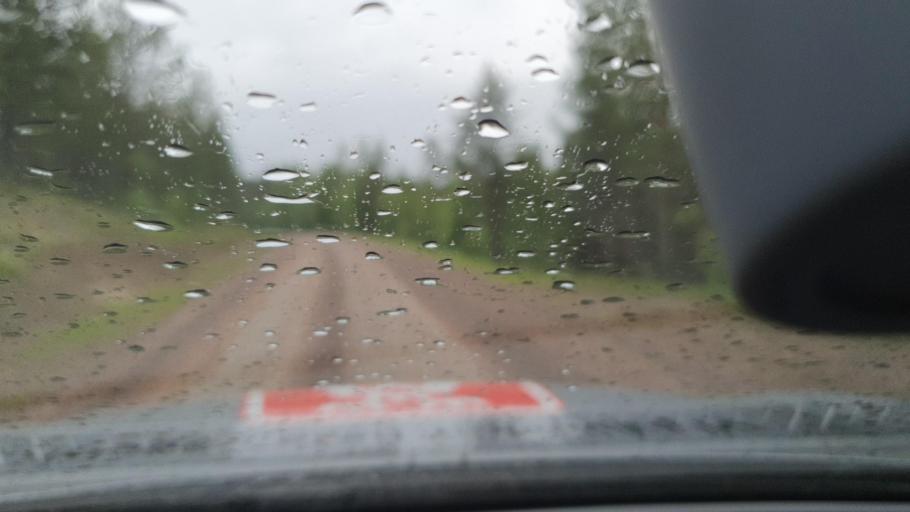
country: SE
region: Norrbotten
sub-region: Overkalix Kommun
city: OEverkalix
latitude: 66.5143
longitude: 22.7485
